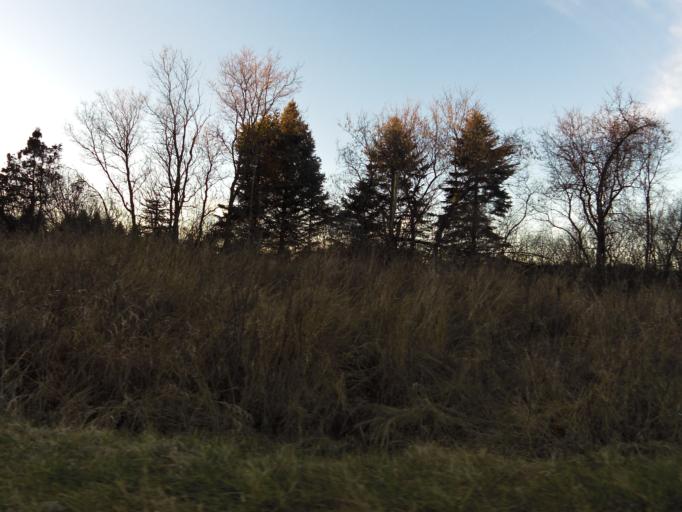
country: US
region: Minnesota
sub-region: Washington County
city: Grant
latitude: 45.0948
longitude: -92.8767
